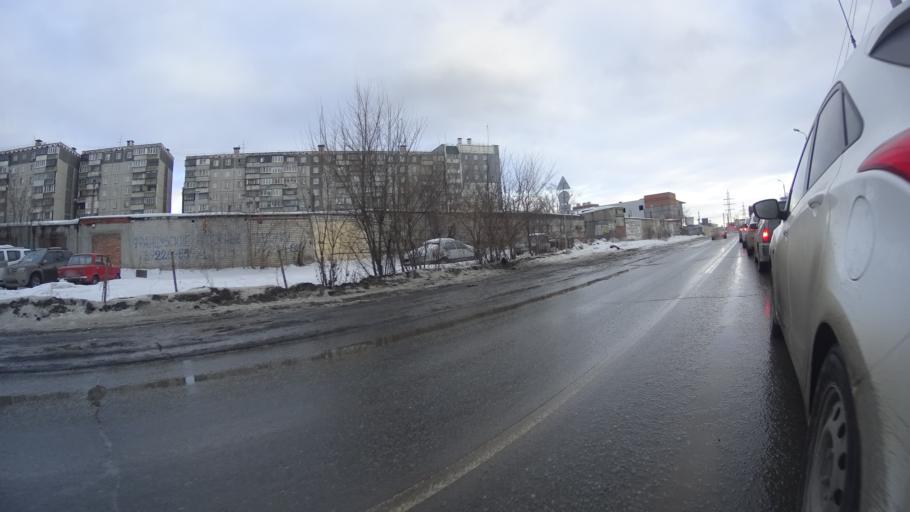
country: RU
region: Chelyabinsk
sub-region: Gorod Chelyabinsk
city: Chelyabinsk
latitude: 55.1397
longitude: 61.4017
